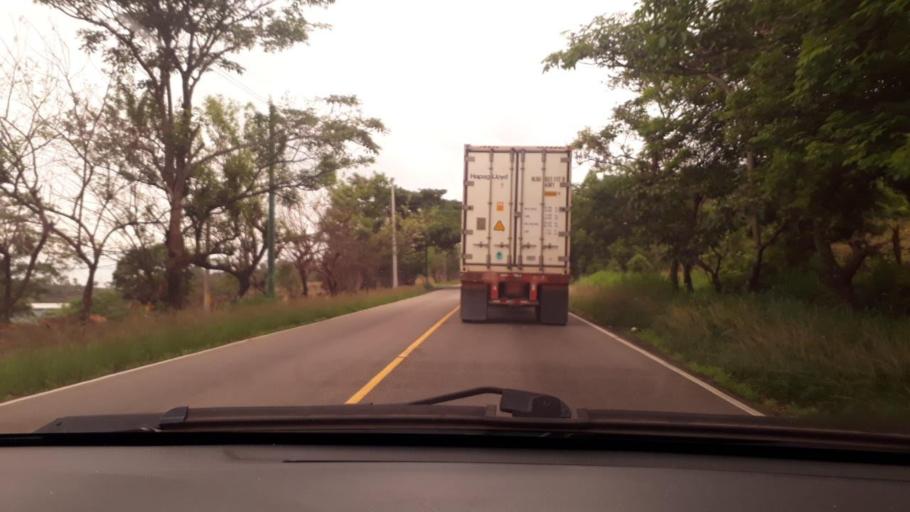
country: GT
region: Chiquimula
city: Quezaltepeque
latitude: 14.5833
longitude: -89.4555
